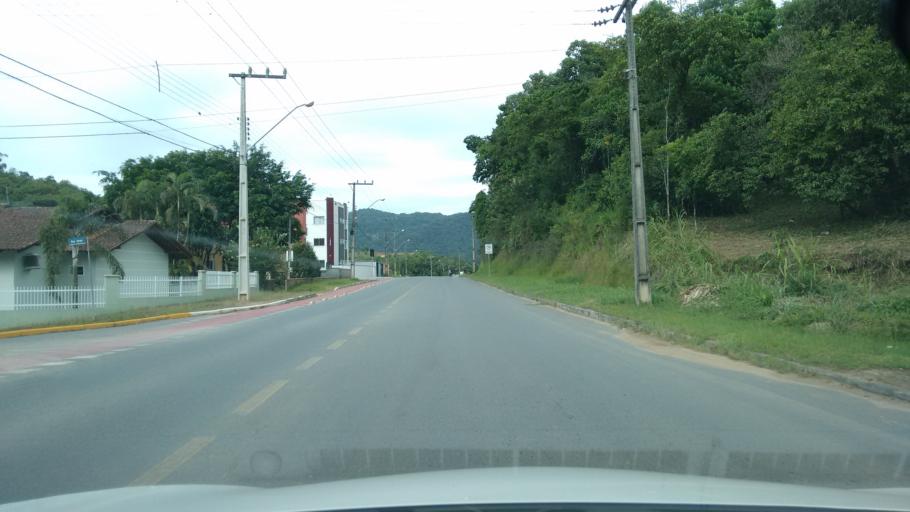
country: BR
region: Santa Catarina
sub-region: Timbo
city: Timbo
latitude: -26.8088
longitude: -49.2632
